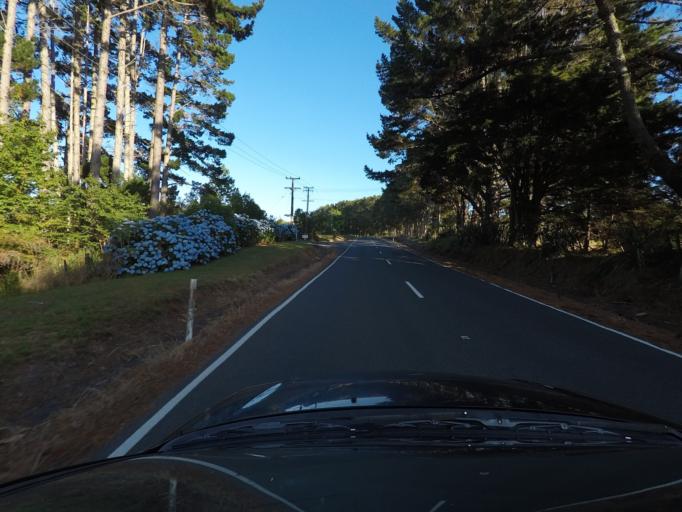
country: NZ
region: Northland
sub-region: Whangarei
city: Whangarei
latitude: -35.6609
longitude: 174.3161
